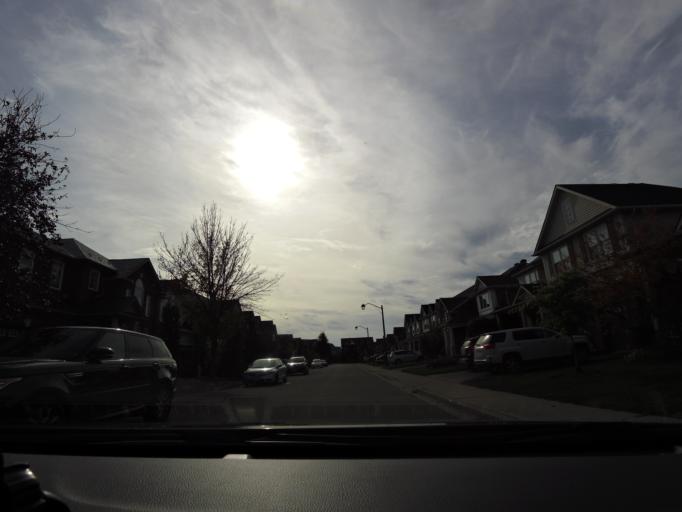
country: CA
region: Ontario
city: Burlington
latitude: 43.4084
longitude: -79.7756
